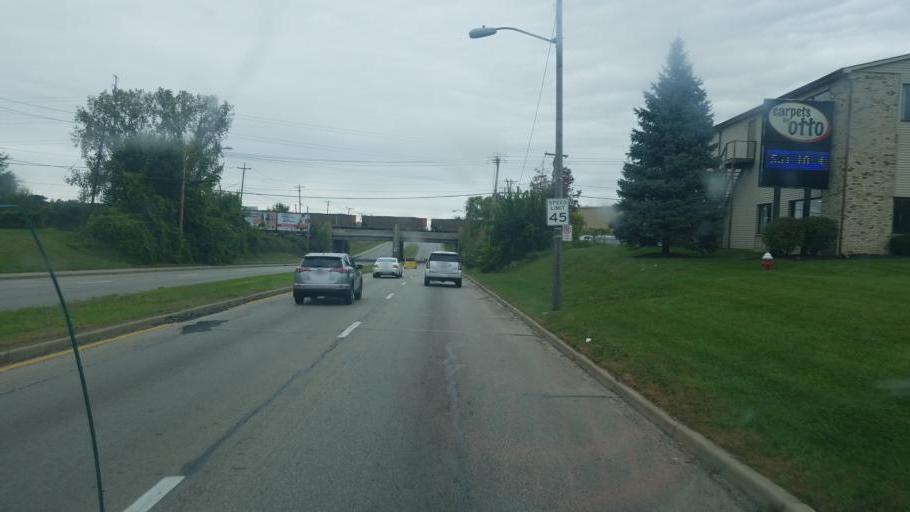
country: US
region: Ohio
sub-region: Lucas County
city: Ottawa Hills
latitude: 41.6233
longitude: -83.6644
